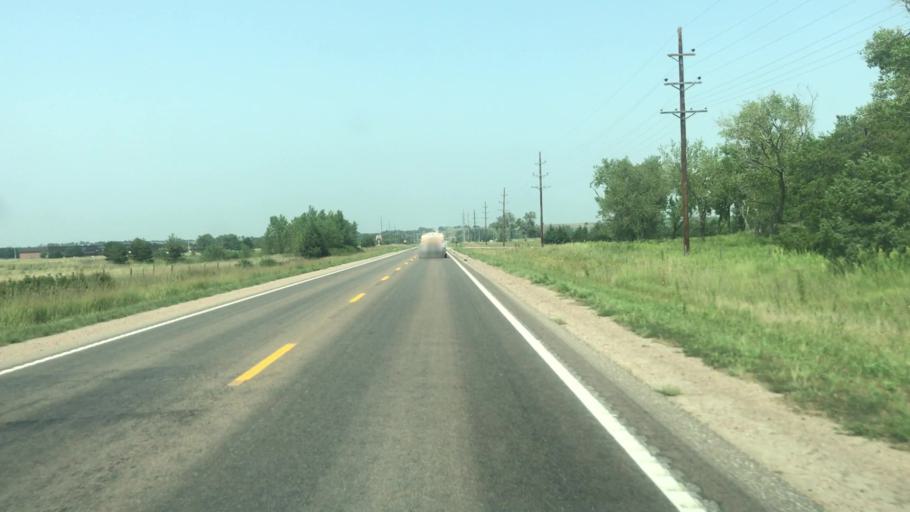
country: US
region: Nebraska
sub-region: Howard County
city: Saint Paul
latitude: 41.0562
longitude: -98.6139
